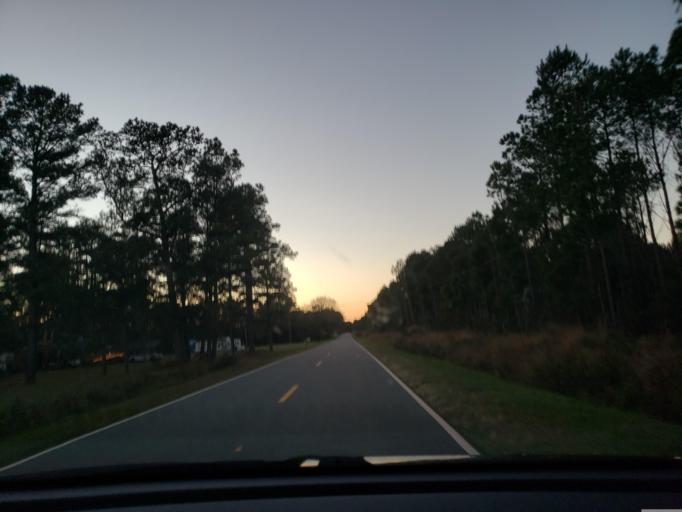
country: US
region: North Carolina
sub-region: Duplin County
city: Beulaville
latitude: 34.7645
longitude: -77.7223
